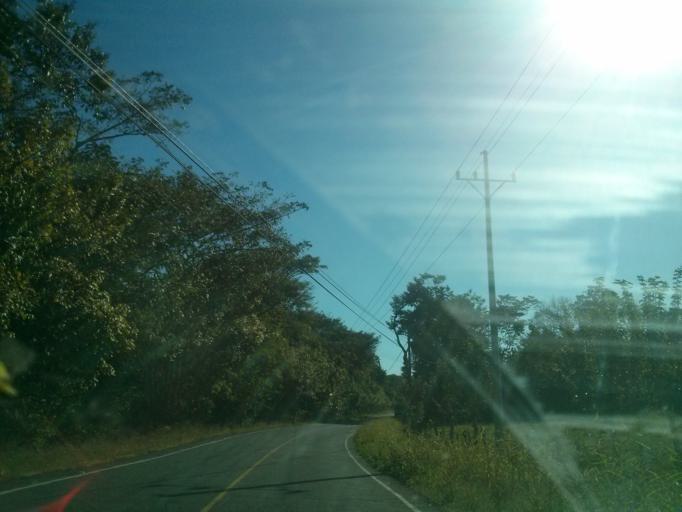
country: CR
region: Puntarenas
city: Paquera
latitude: 9.7024
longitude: -85.0474
